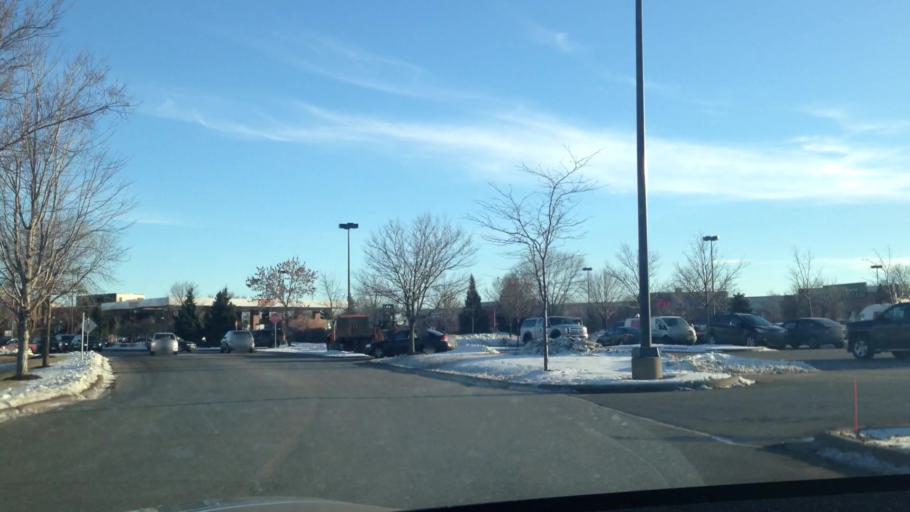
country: US
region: Minnesota
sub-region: Hennepin County
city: Saint Louis Park
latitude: 44.9662
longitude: -93.3514
